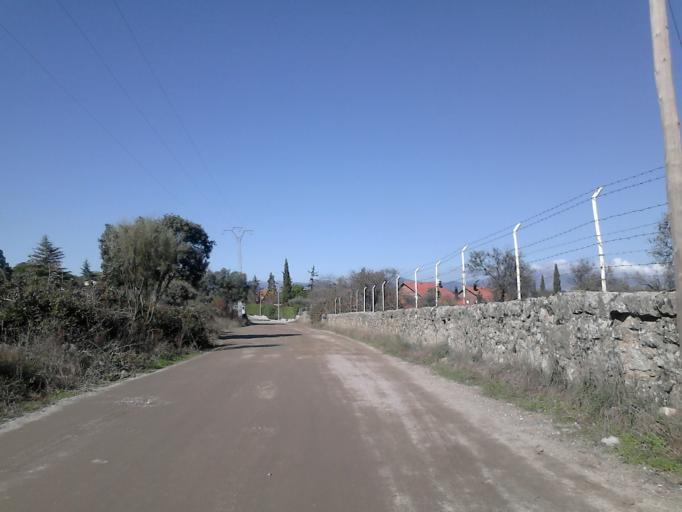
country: ES
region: Madrid
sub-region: Provincia de Madrid
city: Galapagar
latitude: 40.5657
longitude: -3.9958
